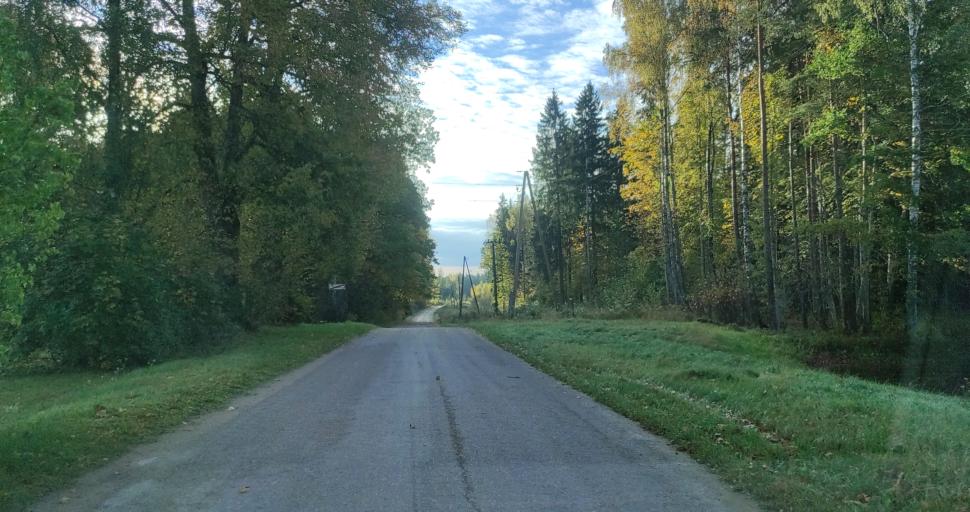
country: LV
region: Skrunda
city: Skrunda
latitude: 56.7409
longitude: 21.8817
